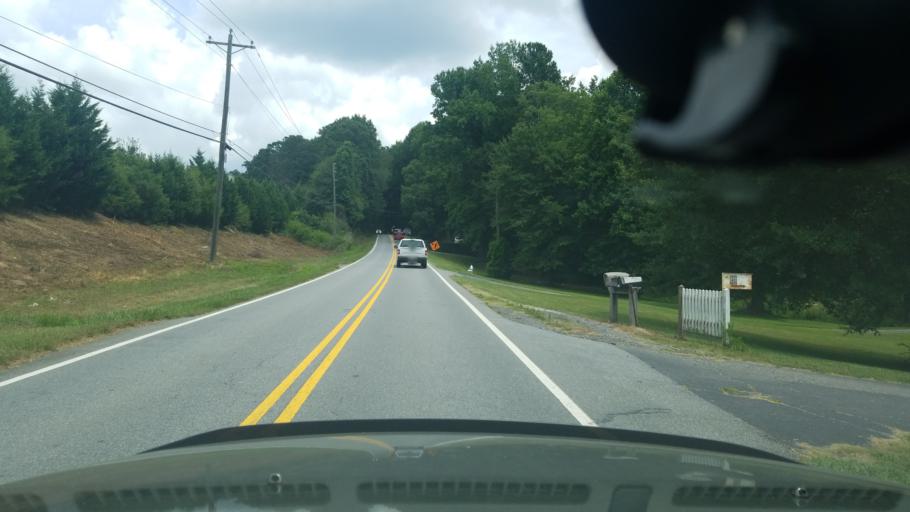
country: US
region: Georgia
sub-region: Forsyth County
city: Cumming
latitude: 34.1935
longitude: -84.2249
